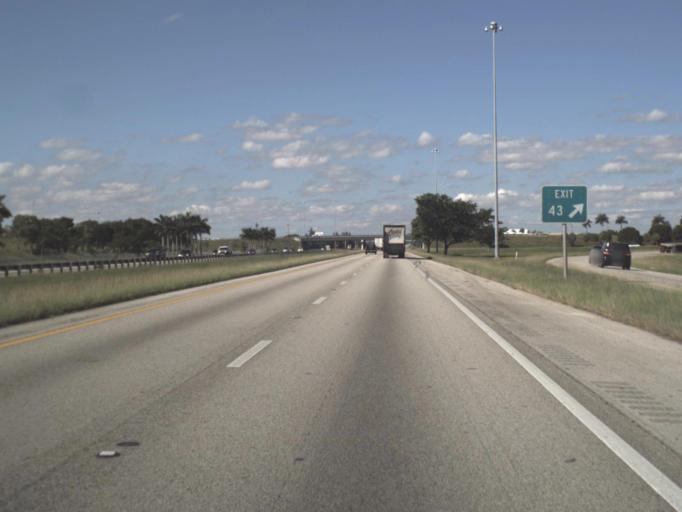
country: US
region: Florida
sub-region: Miami-Dade County
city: Country Club
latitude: 25.9712
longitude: -80.2896
